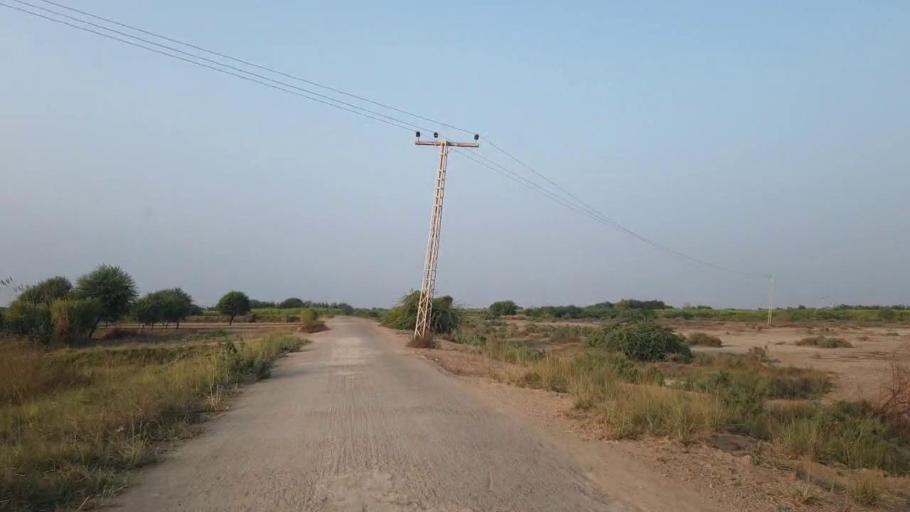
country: PK
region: Sindh
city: Tando Ghulam Ali
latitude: 25.0768
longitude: 68.9595
